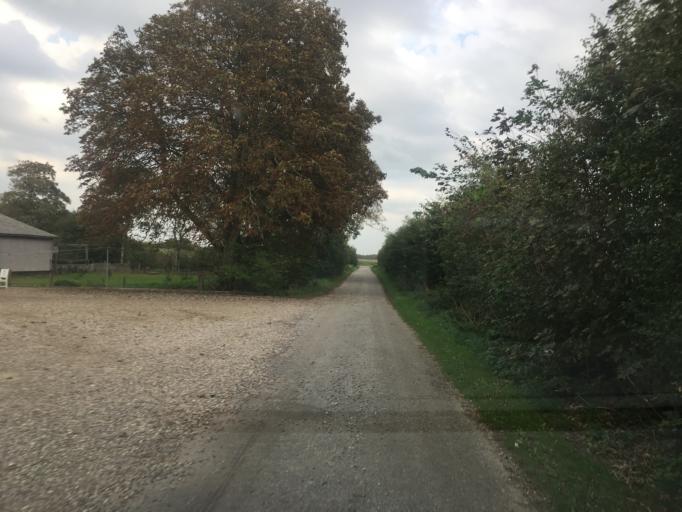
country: DK
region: South Denmark
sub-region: Tonder Kommune
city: Logumkloster
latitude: 55.0026
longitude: 9.0457
